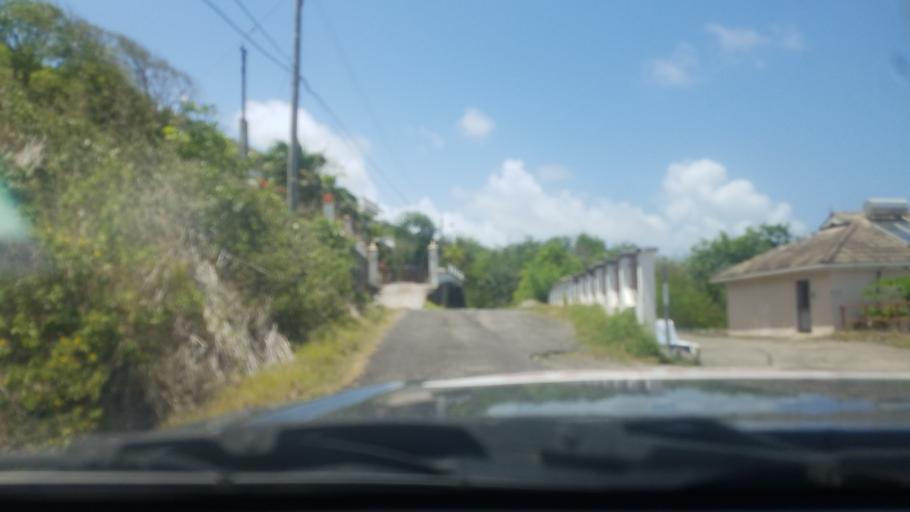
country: LC
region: Vieux-Fort
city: Vieux Fort
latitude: 13.7378
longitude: -60.9441
